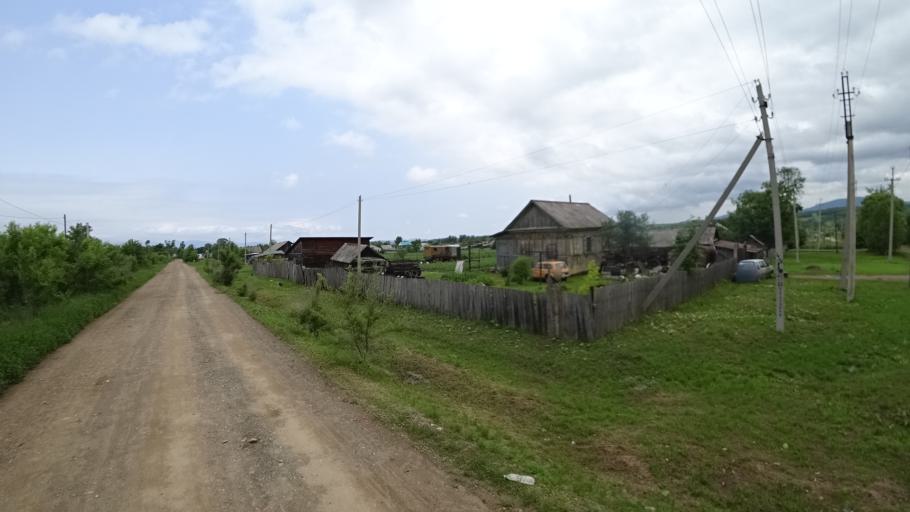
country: RU
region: Primorskiy
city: Novosysoyevka
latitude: 44.2334
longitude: 133.3651
